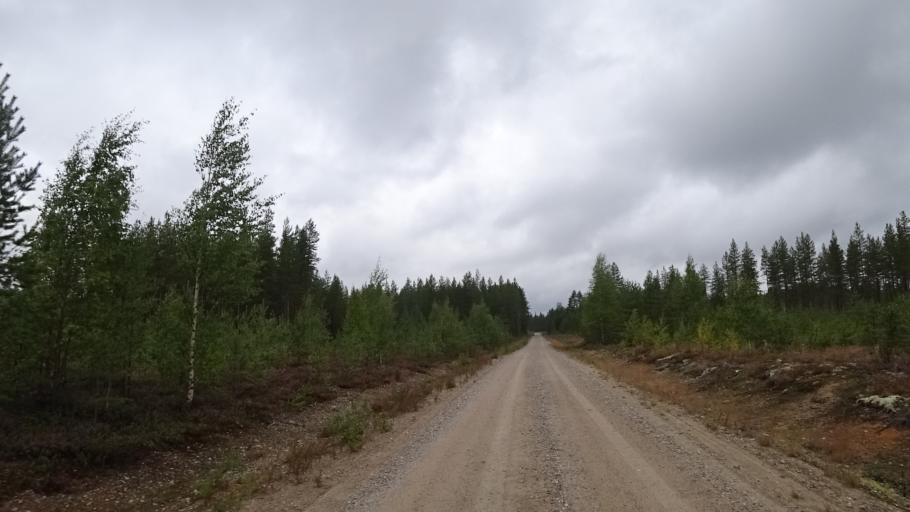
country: FI
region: North Karelia
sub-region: Pielisen Karjala
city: Lieksa
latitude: 63.5191
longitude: 30.1091
